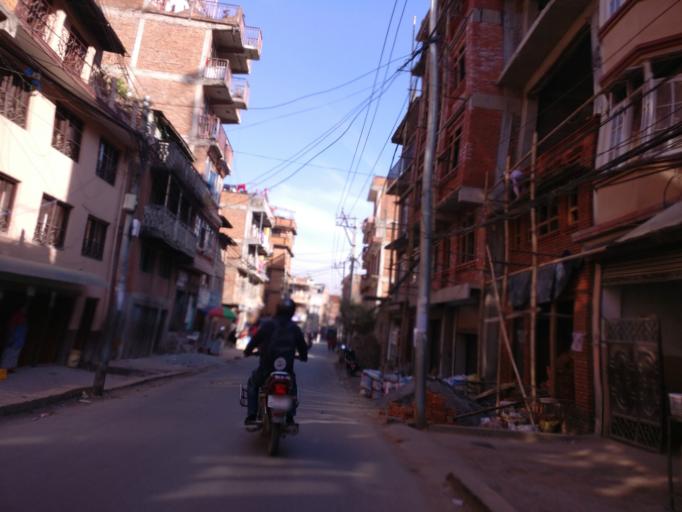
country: NP
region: Central Region
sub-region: Bagmati Zone
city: Patan
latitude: 27.6728
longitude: 85.3287
